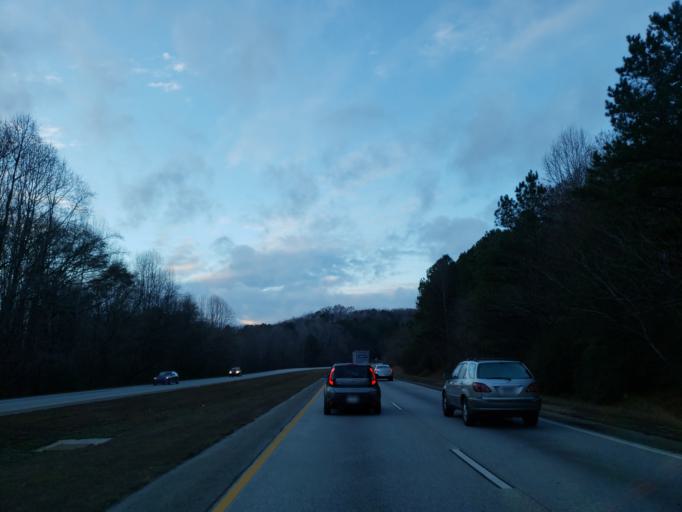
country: US
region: Georgia
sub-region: Fulton County
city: Union City
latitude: 33.6710
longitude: -84.5493
